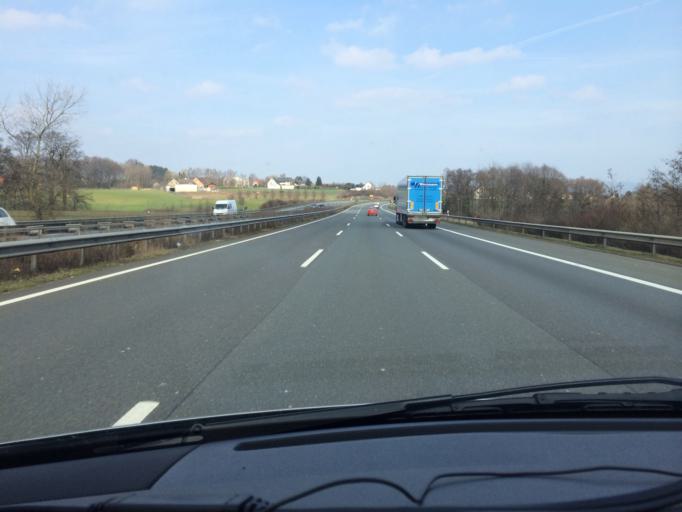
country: DE
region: North Rhine-Westphalia
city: Bad Oeynhausen
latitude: 52.1685
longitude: 8.8147
